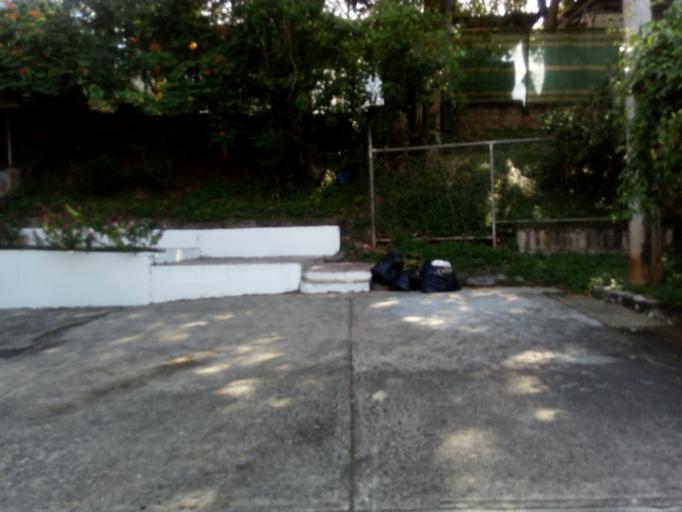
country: PA
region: Panama
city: Panama
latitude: 8.9957
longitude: -79.5375
